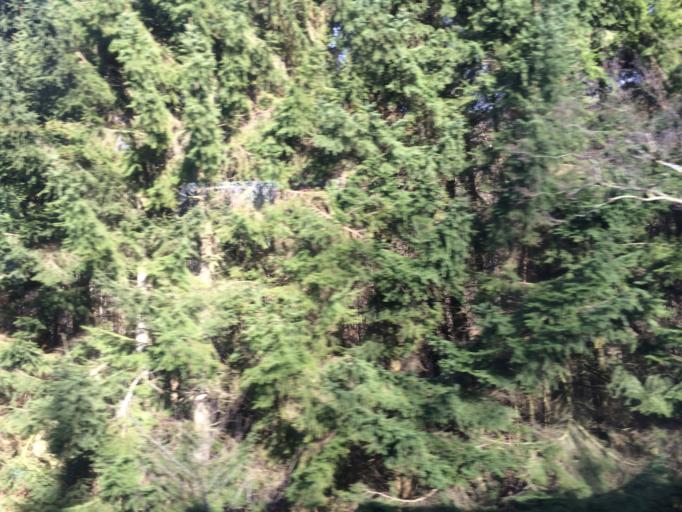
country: DK
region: South Denmark
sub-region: Vejle Kommune
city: Vejle
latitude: 55.7595
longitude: 9.5177
